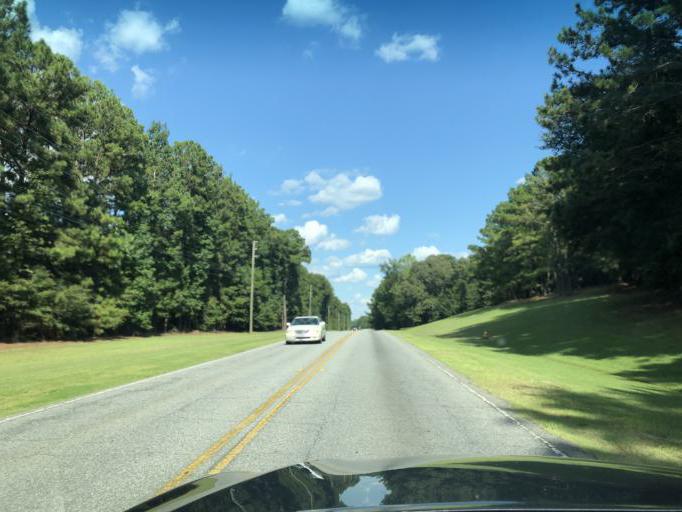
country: US
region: Georgia
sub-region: Muscogee County
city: Columbus
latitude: 32.5200
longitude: -84.9043
